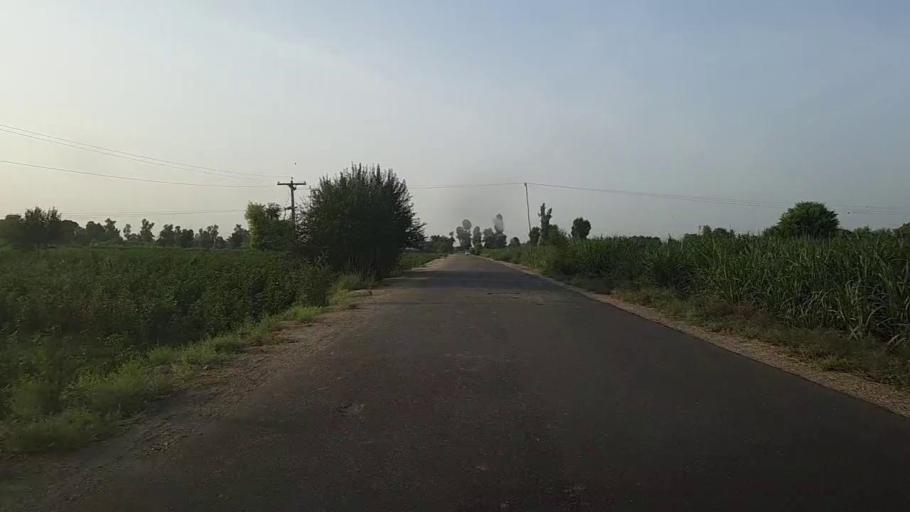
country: PK
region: Sindh
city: Ubauro
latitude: 28.1854
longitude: 69.8279
